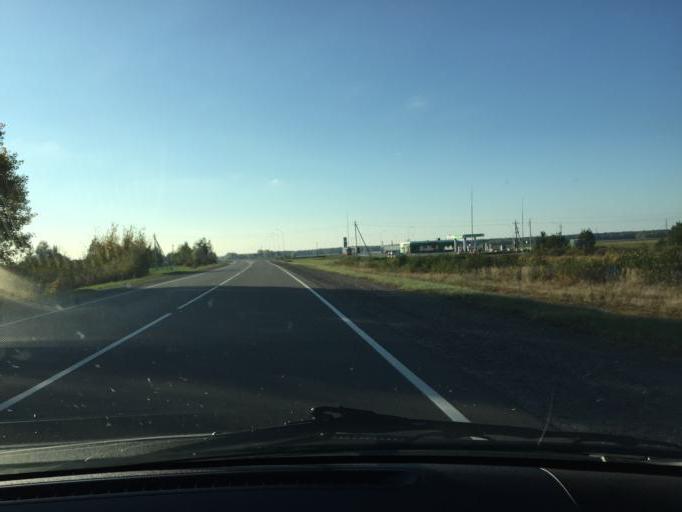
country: BY
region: Brest
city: Horad Luninyets
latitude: 52.3165
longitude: 26.6345
